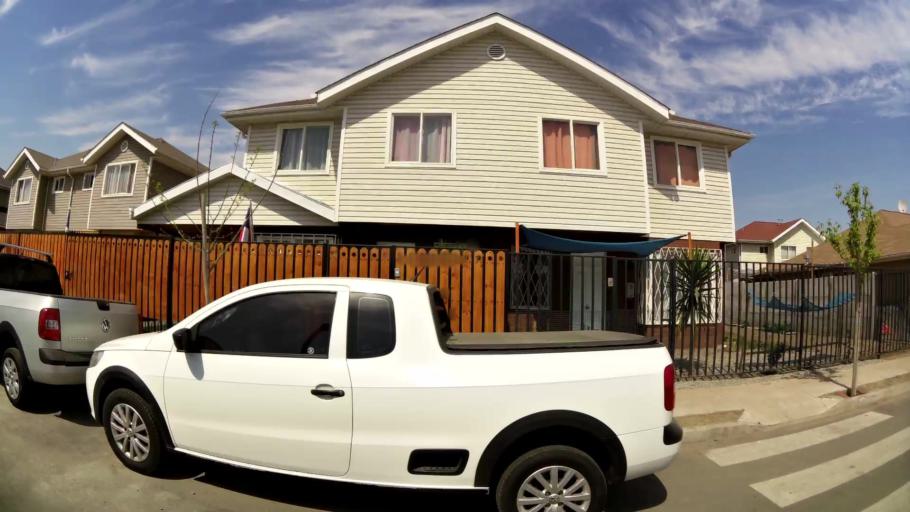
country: CL
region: Santiago Metropolitan
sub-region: Provincia de Cordillera
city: Puente Alto
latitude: -33.5933
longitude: -70.5990
